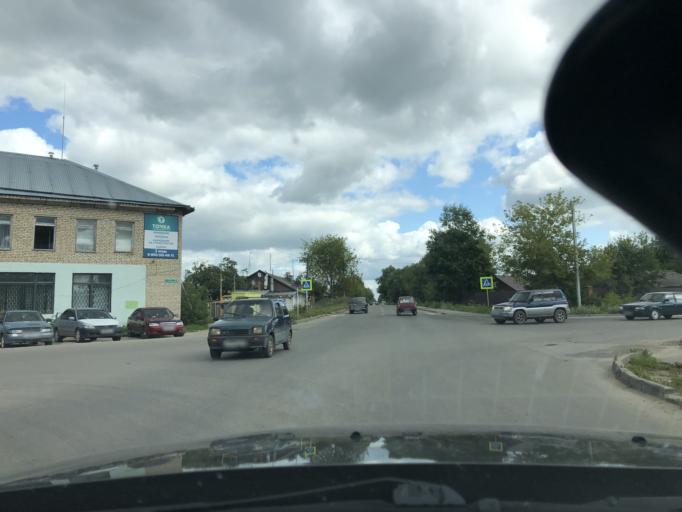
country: RU
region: Tula
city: Yasnogorsk
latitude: 54.4814
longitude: 37.6991
